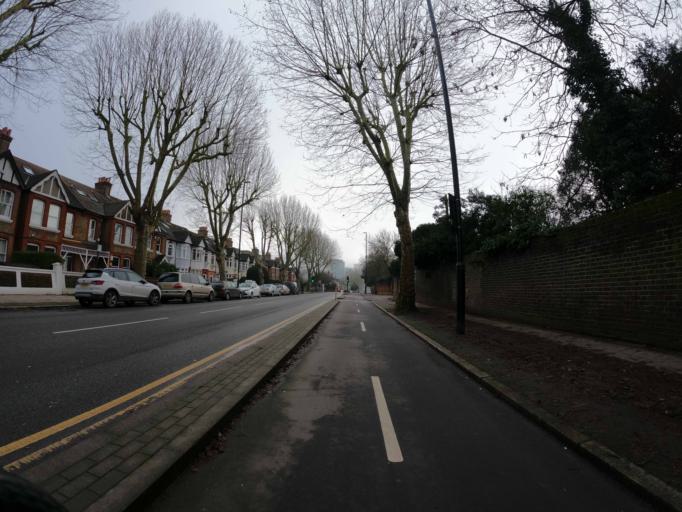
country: GB
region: England
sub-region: Greater London
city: Brentford
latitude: 51.4929
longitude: -0.3184
